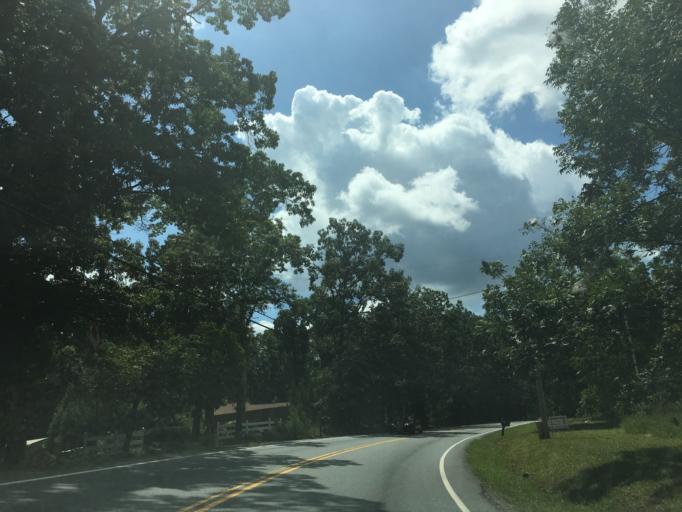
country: US
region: Georgia
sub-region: Fulton County
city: Roswell
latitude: 34.0939
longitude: -84.3633
